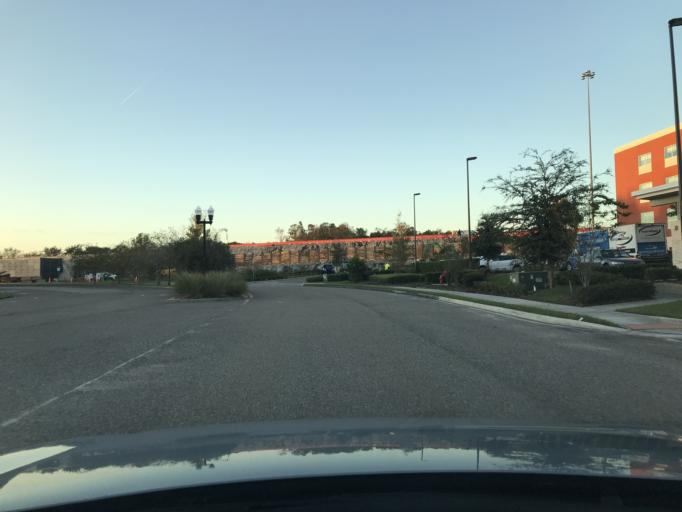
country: US
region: Florida
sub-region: Hillsborough County
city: Pebble Creek
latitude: 28.1944
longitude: -82.3810
